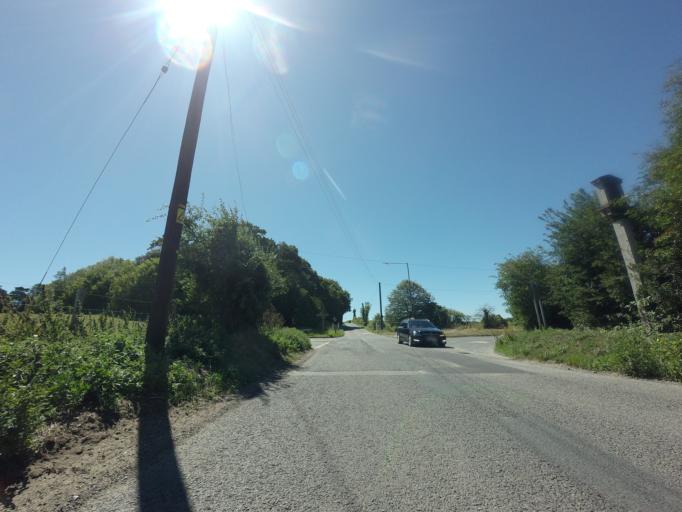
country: GB
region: England
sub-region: Kent
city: Eastry
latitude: 51.2395
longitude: 1.3076
